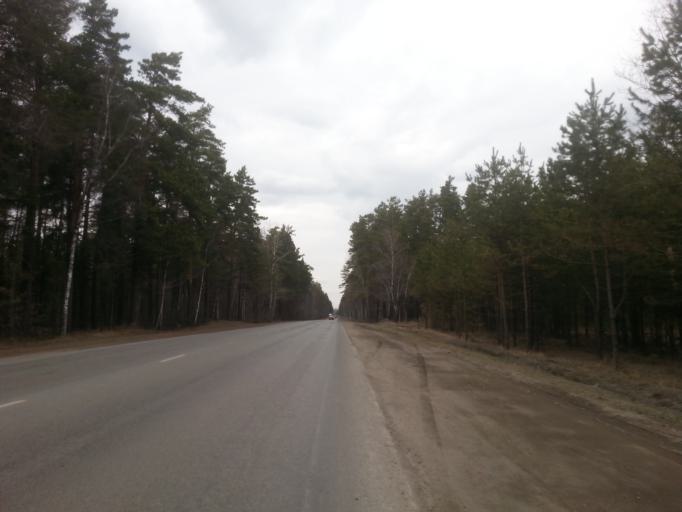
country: RU
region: Altai Krai
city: Yuzhnyy
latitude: 53.2743
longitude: 83.7218
